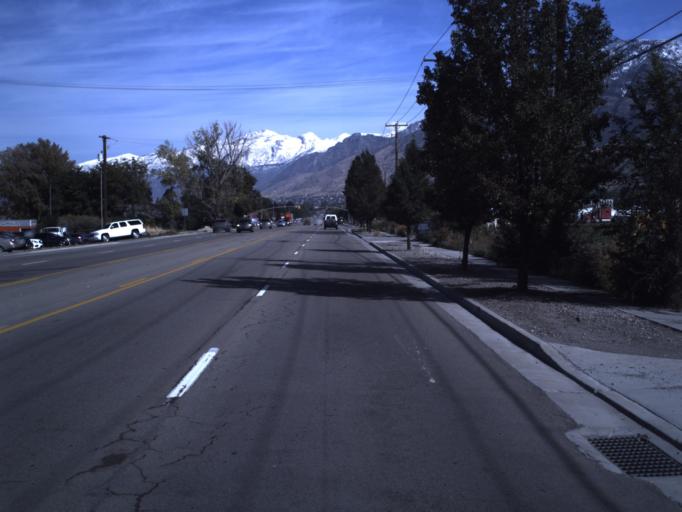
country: US
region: Utah
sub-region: Utah County
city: Pleasant Grove
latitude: 40.3479
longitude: -111.7407
